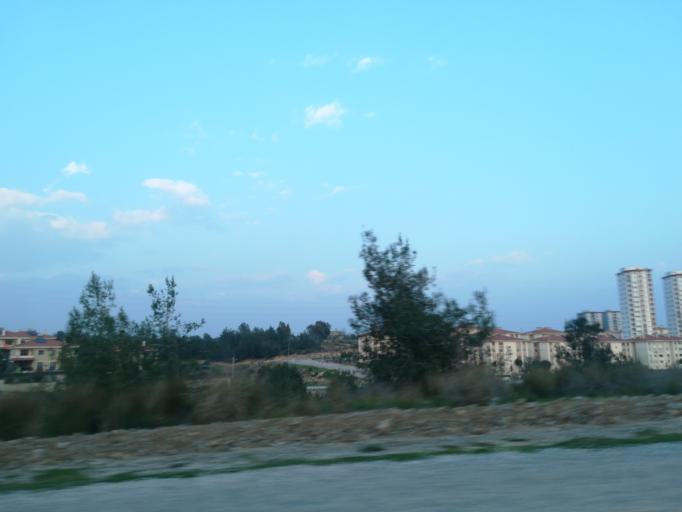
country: TR
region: Adana
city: Adana
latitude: 37.0808
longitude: 35.4096
